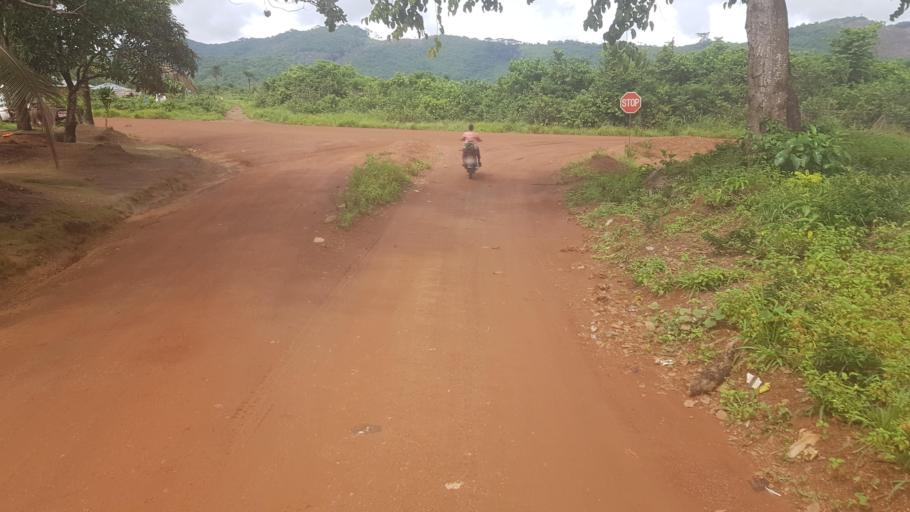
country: SL
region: Southern Province
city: Mogbwemo
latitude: 7.7524
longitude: -12.3086
